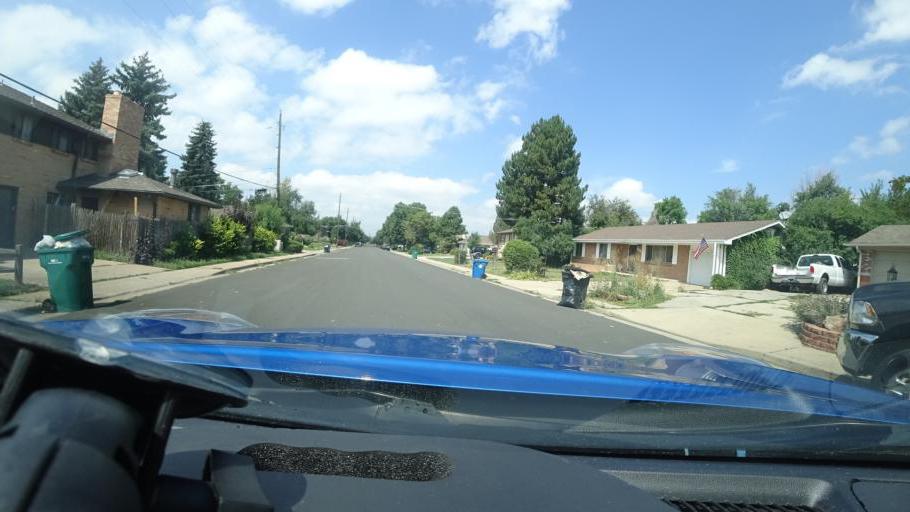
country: US
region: Colorado
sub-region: Adams County
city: Aurora
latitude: 39.7250
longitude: -104.8530
